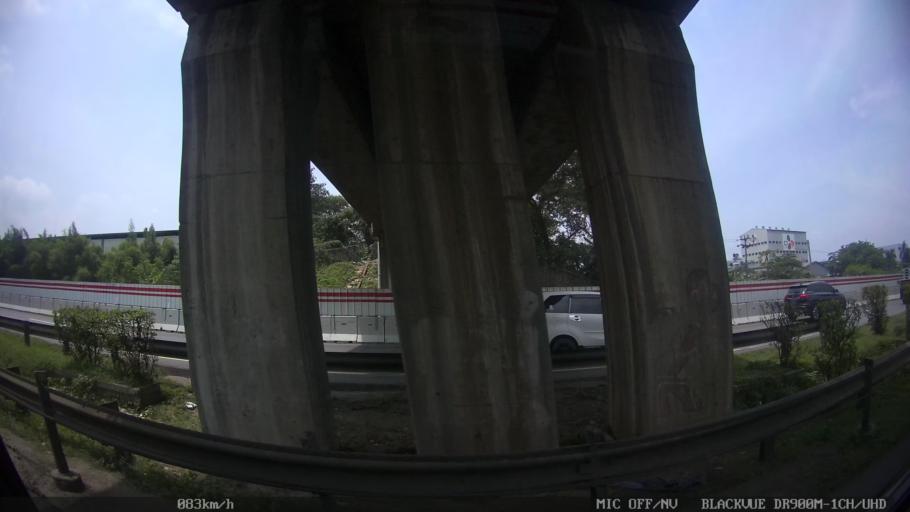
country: ID
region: West Java
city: Kresek
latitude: -6.1677
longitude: 106.3390
